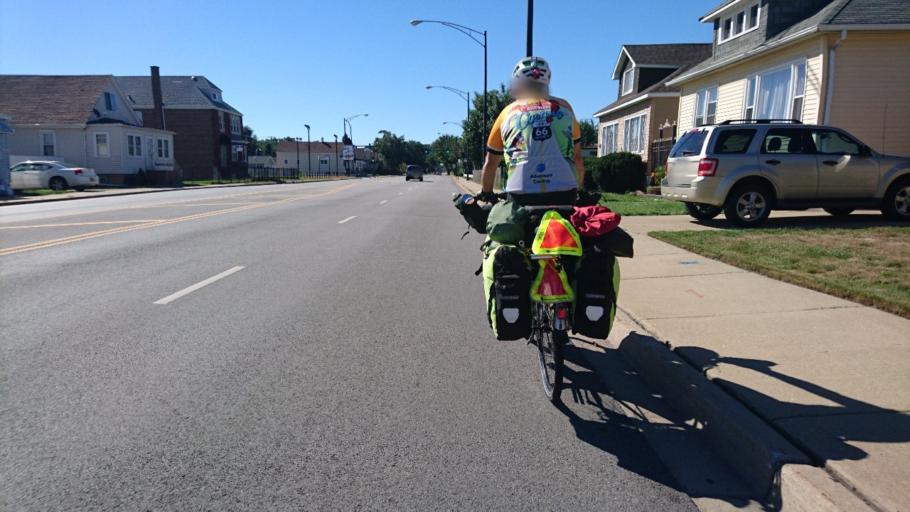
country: US
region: Illinois
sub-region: Cook County
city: Burnham
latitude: 41.6530
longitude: -87.5400
